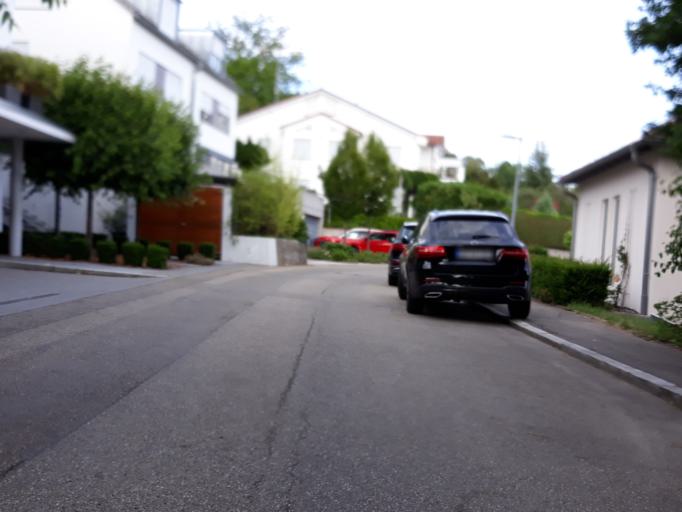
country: DE
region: Baden-Wuerttemberg
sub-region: Regierungsbezirk Stuttgart
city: Sindelfingen
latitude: 48.6888
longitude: 9.0275
